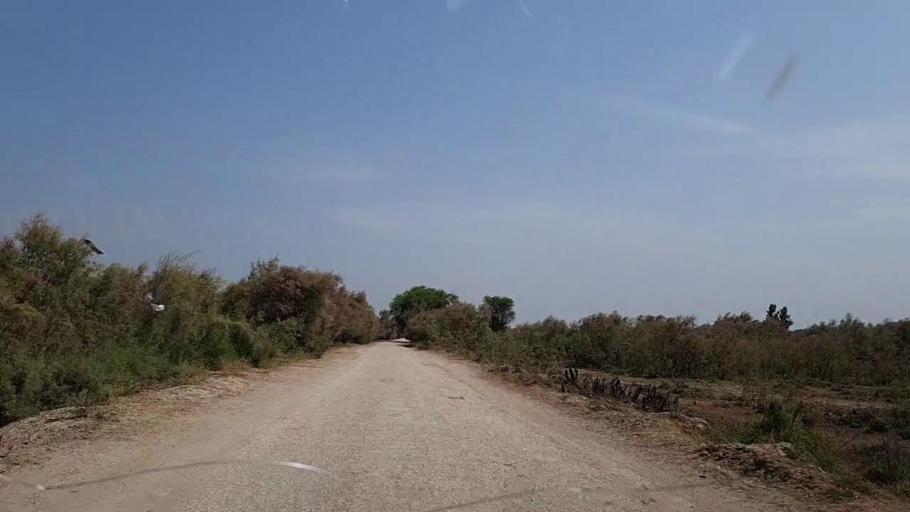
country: PK
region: Sindh
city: Khanpur
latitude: 27.8213
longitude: 69.3039
